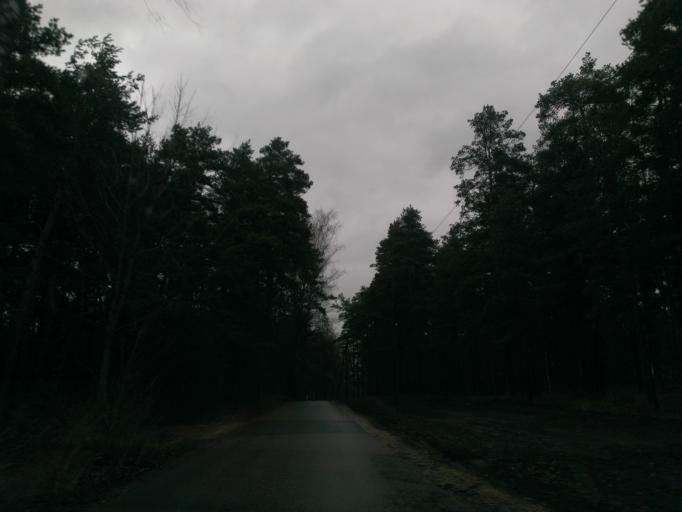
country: LV
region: Adazi
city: Adazi
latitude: 57.0323
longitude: 24.3218
